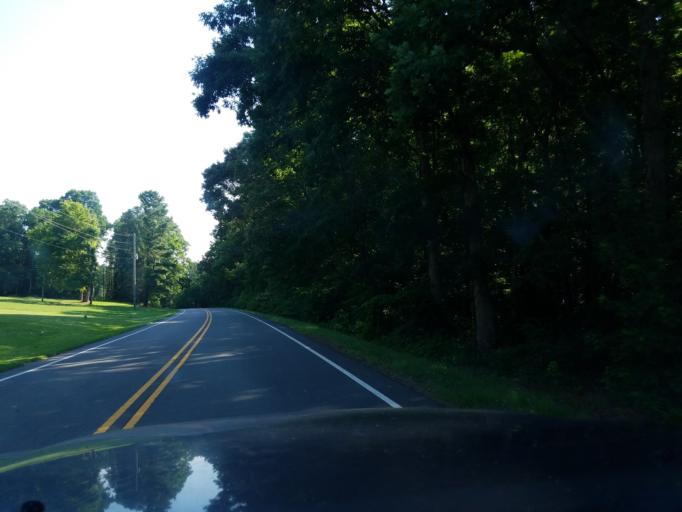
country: US
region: North Carolina
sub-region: Granville County
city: Creedmoor
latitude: 36.2348
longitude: -78.6986
